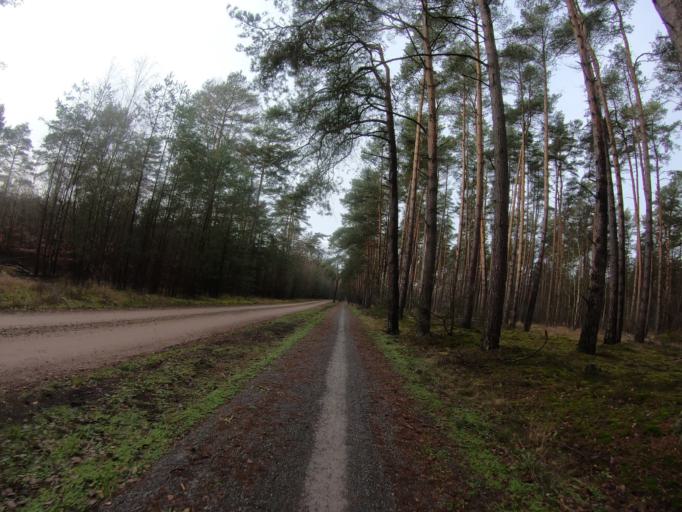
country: DE
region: Lower Saxony
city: Wagenhoff
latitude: 52.5112
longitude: 10.4515
